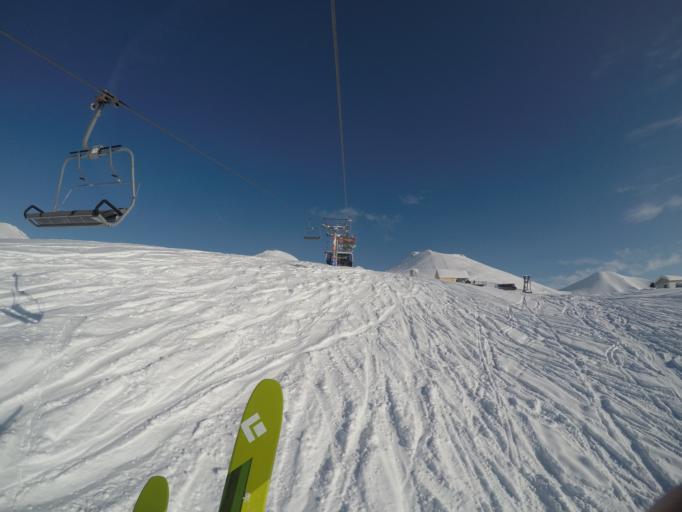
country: GE
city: Gudauri
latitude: 42.4888
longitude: 44.4985
